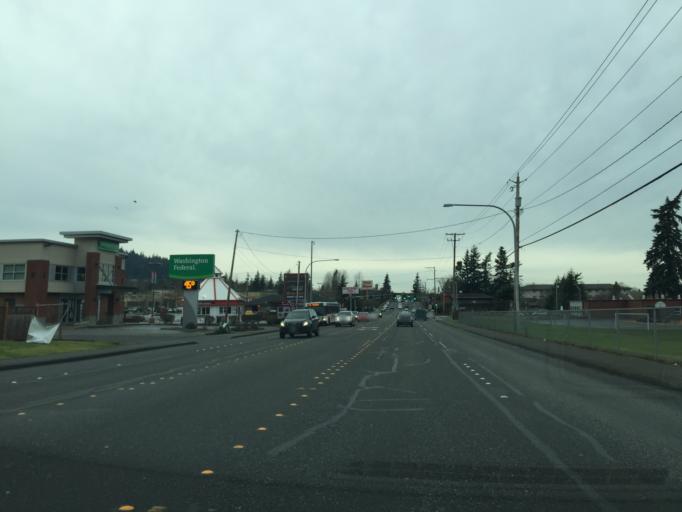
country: US
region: Washington
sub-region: Whatcom County
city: Bellingham
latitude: 48.7450
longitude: -122.4600
